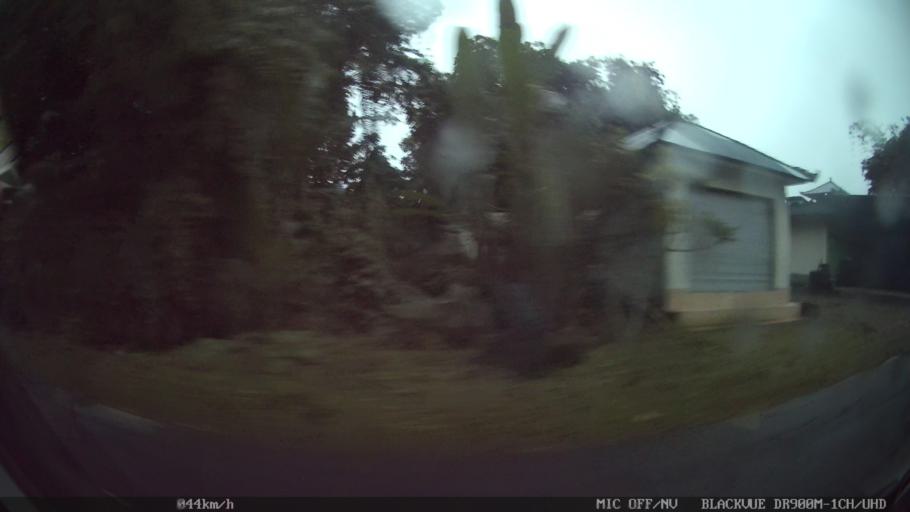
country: ID
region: Bali
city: Banjar Taro Kelod
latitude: -8.3592
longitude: 115.2738
